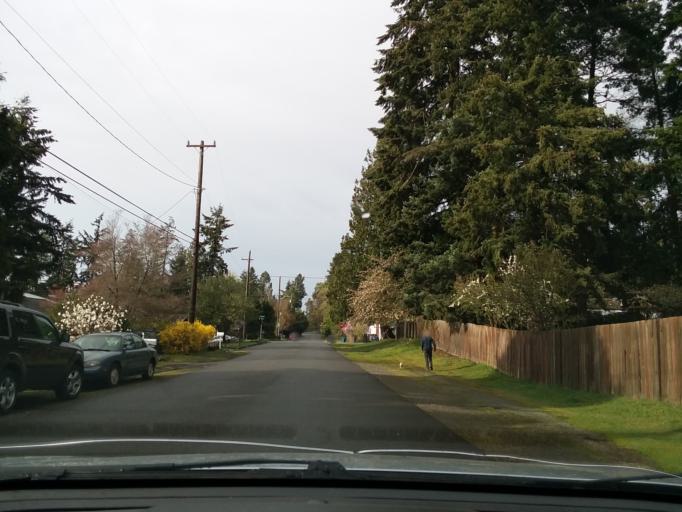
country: US
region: Washington
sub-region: King County
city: Shoreline
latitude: 47.7429
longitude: -122.3265
